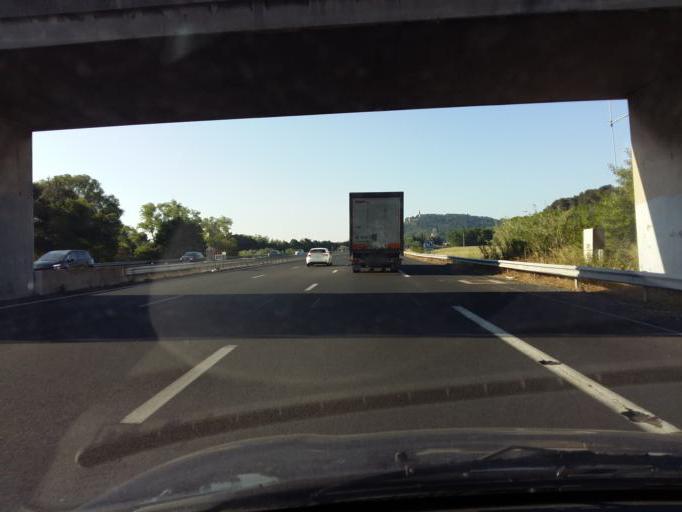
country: FR
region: Provence-Alpes-Cote d'Azur
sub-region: Departement des Bouches-du-Rhone
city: Orgon
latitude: 43.8065
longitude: 5.0390
